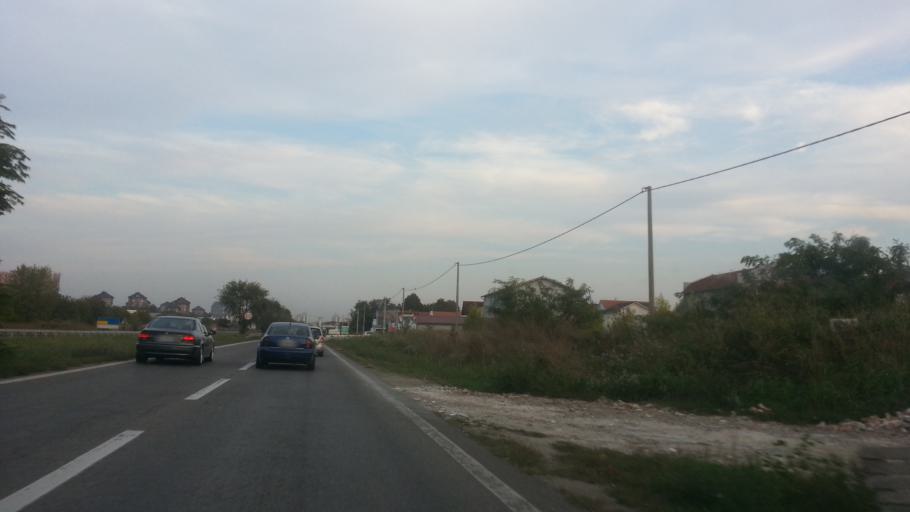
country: RS
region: Central Serbia
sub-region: Belgrade
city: Zemun
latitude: 44.8605
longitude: 20.3544
